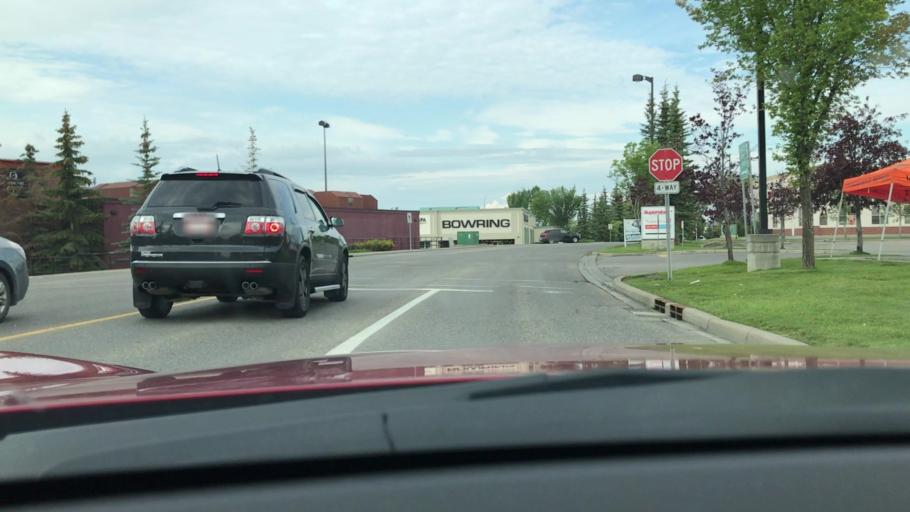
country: CA
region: Alberta
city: Calgary
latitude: 51.0181
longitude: -114.1731
